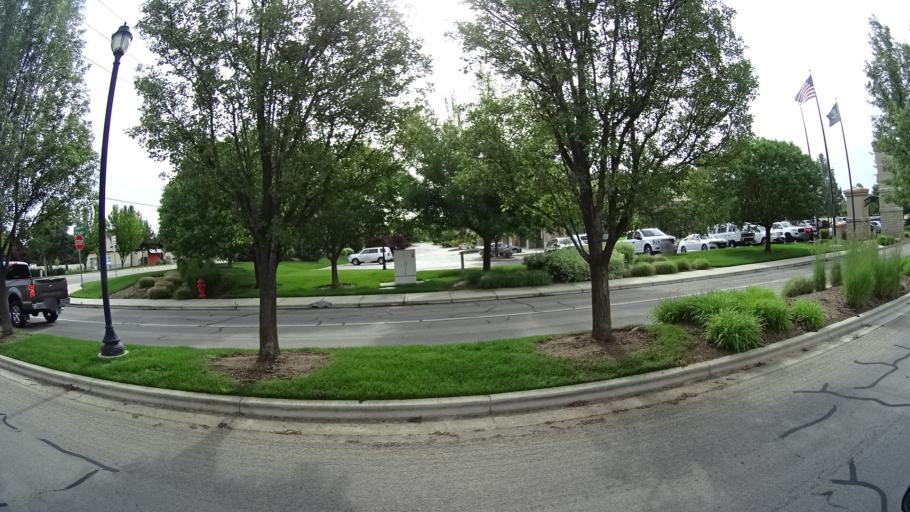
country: US
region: Idaho
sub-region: Ada County
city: Meridian
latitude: 43.5901
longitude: -116.3584
